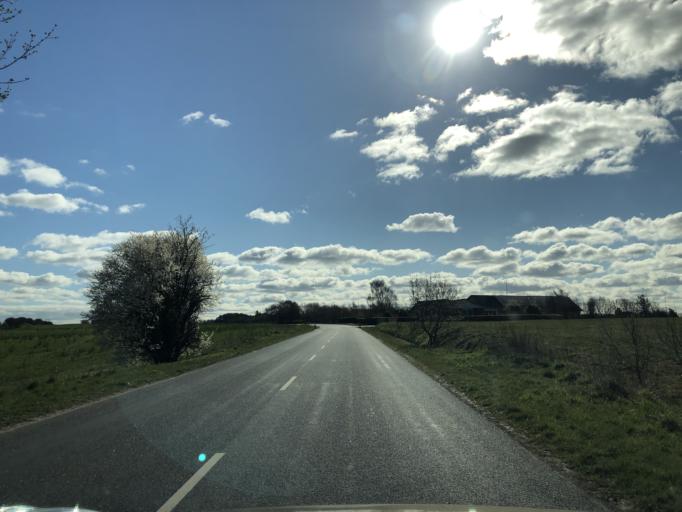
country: DK
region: North Denmark
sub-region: Vesthimmerland Kommune
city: Alestrup
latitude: 56.6064
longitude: 9.5547
